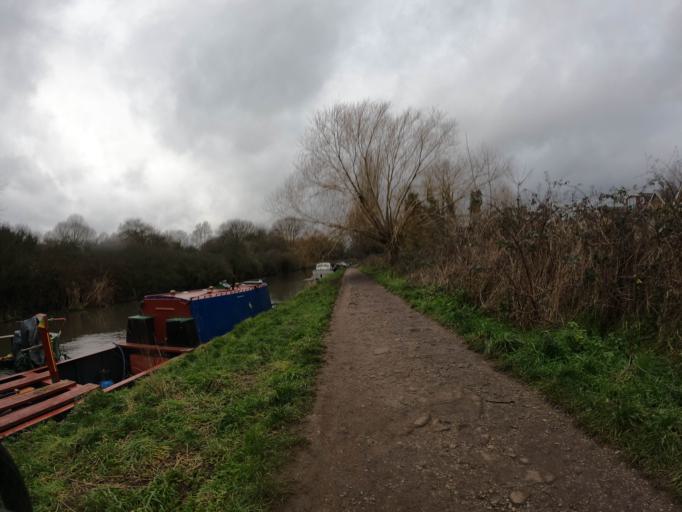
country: GB
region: England
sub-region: Greater London
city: Isleworth
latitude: 51.5031
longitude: -0.3417
